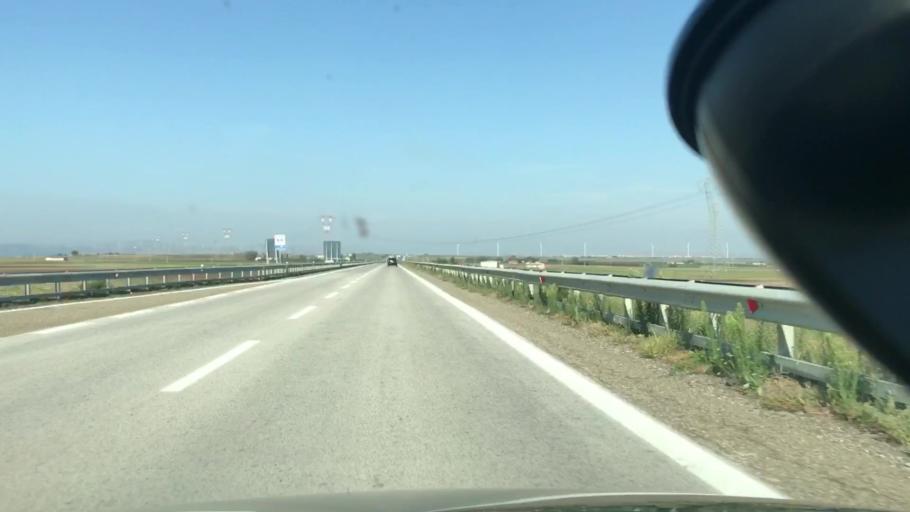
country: IT
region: Basilicate
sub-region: Provincia di Potenza
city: Venosa
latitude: 40.9962
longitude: 15.8804
